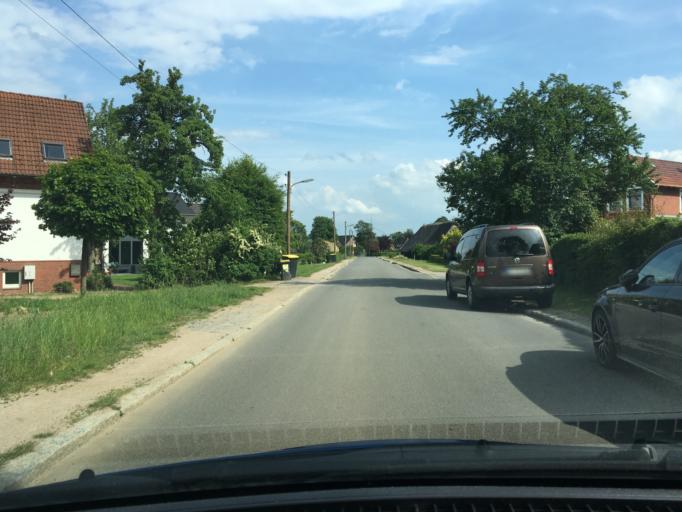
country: DE
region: Hamburg
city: Bergedorf
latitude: 53.4696
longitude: 10.2351
